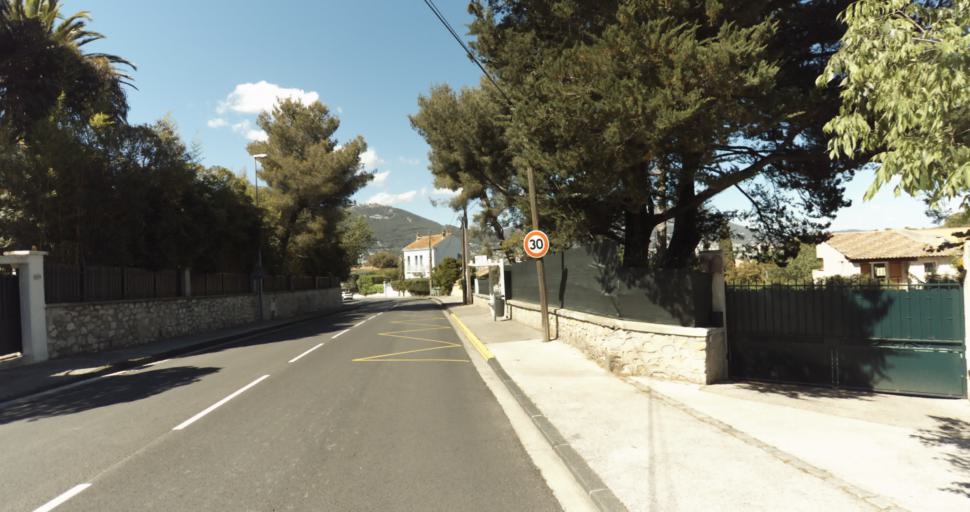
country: FR
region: Provence-Alpes-Cote d'Azur
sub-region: Departement du Var
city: La Valette-du-Var
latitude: 43.1108
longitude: 5.9691
